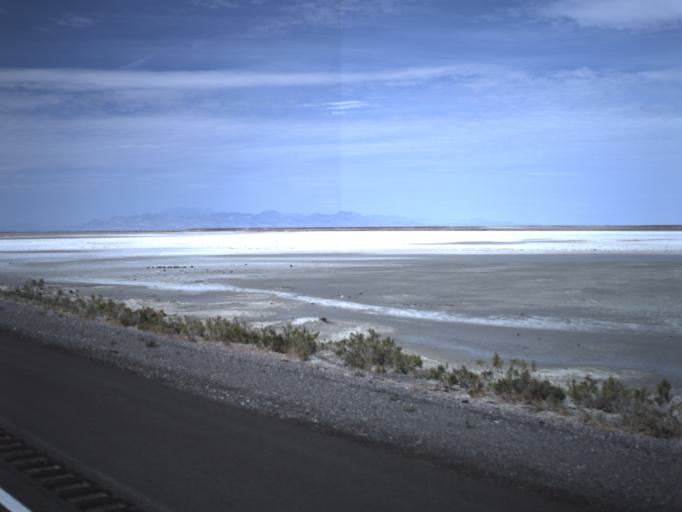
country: US
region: Utah
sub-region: Tooele County
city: Wendover
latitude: 40.7286
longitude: -113.3413
